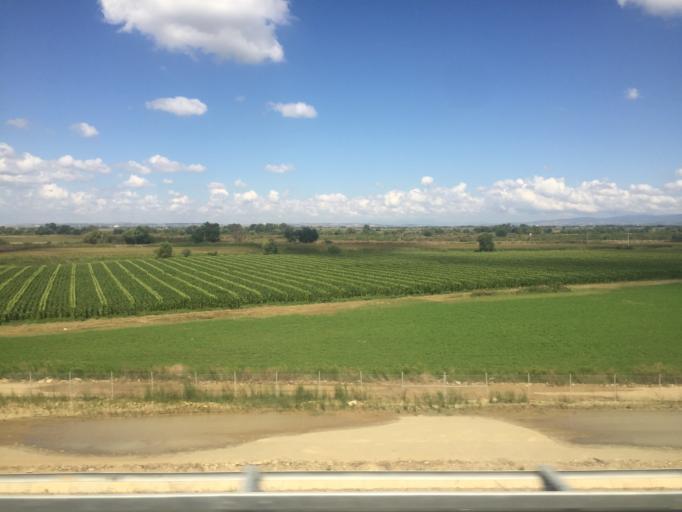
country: TR
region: Bursa
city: Karacabey
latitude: 40.1297
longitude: 28.2893
